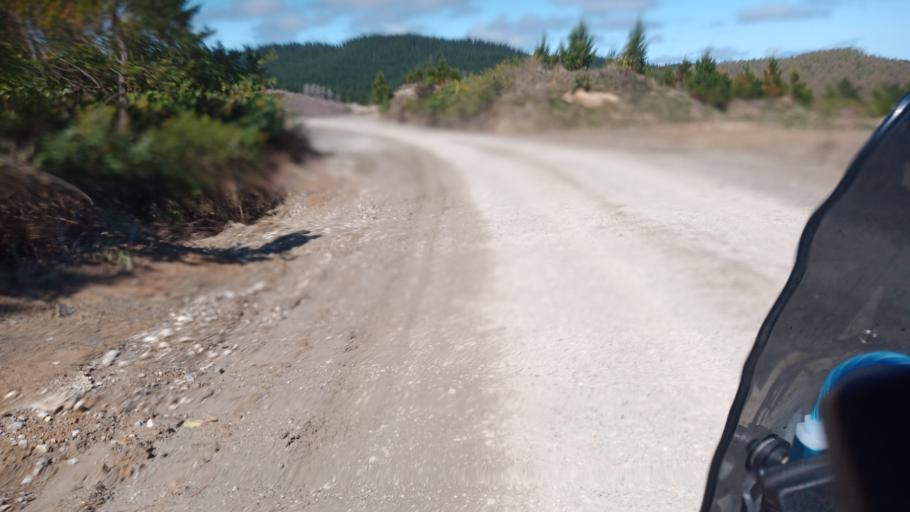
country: NZ
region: Gisborne
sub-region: Gisborne District
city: Gisborne
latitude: -38.9087
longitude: 177.8074
